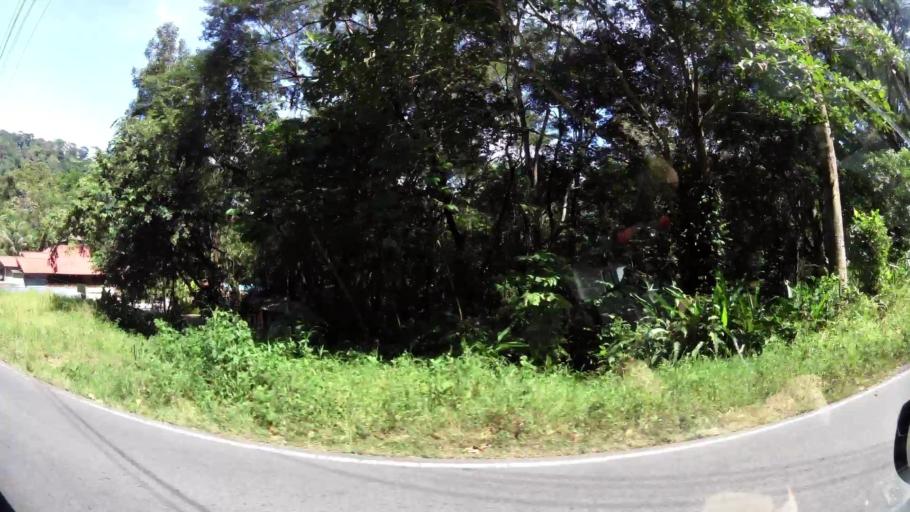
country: CR
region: San Jose
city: San Isidro
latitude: 9.2647
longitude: -83.8635
